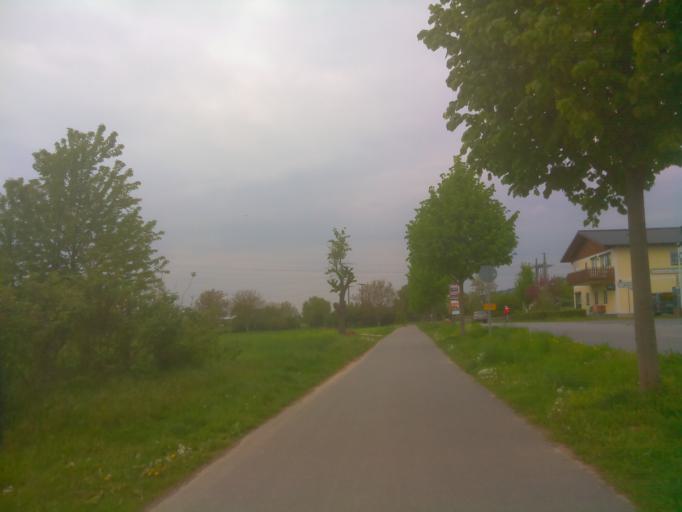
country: DE
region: Baden-Wuerttemberg
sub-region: Karlsruhe Region
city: Dossenheim
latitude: 49.4544
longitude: 8.6636
